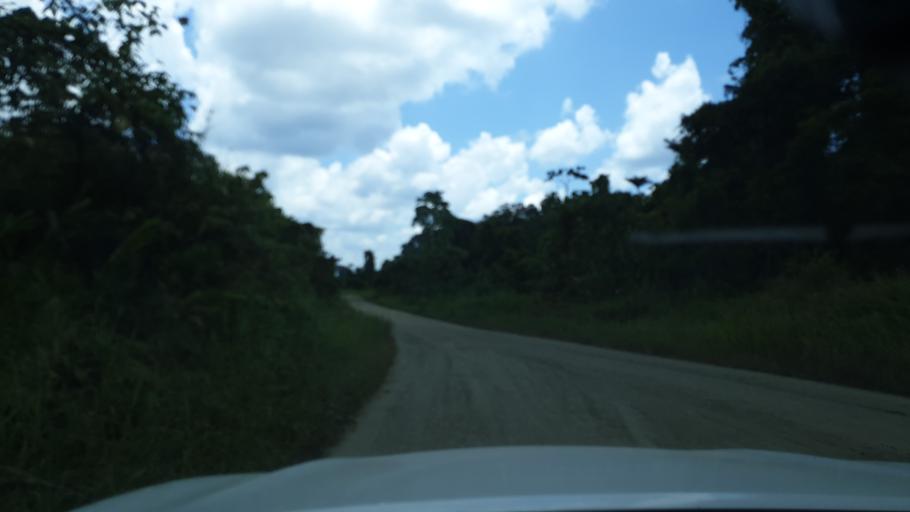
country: PG
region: East Sepik
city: Angoram
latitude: -3.8230
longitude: 143.8558
